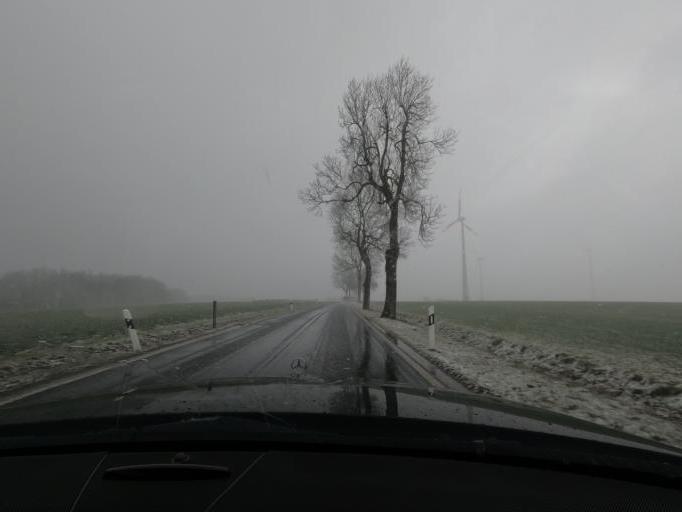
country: DE
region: Thuringia
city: Buttstedt
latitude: 51.2441
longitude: 10.2822
